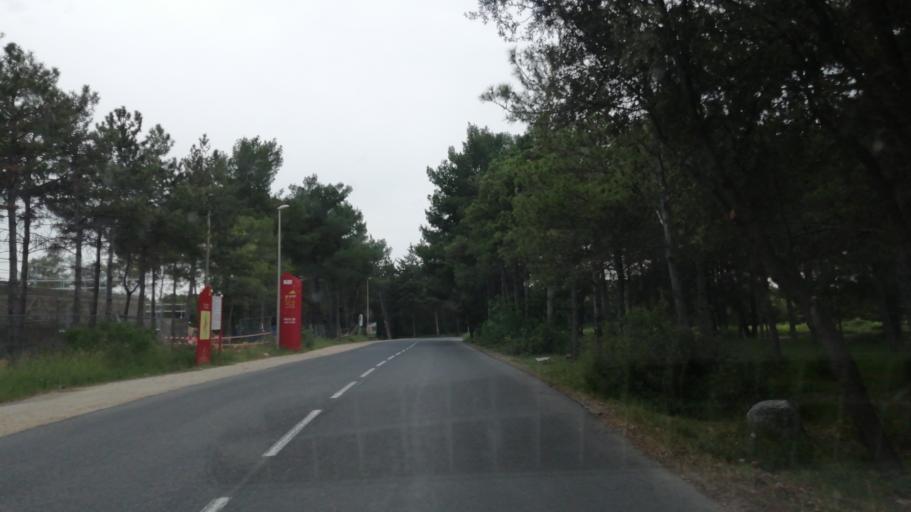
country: FR
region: Languedoc-Roussillon
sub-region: Departement de l'Herault
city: Saint-Mathieu-de-Treviers
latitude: 43.7615
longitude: 3.8701
